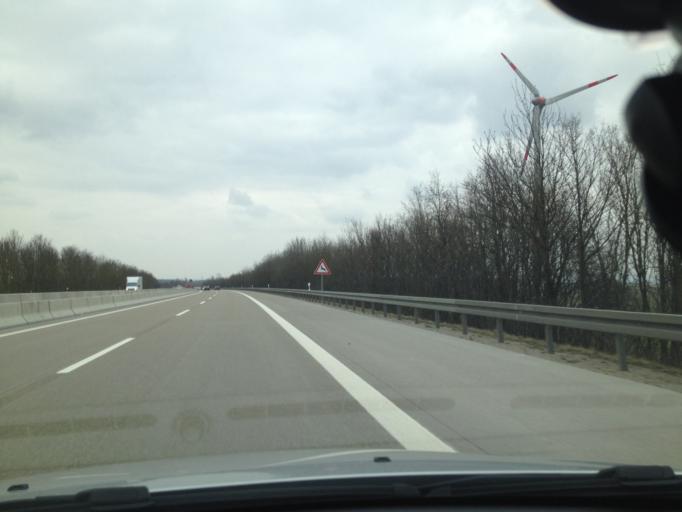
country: DE
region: Bavaria
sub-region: Regierungsbezirk Mittelfranken
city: Gollhofen
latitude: 49.5948
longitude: 10.1745
